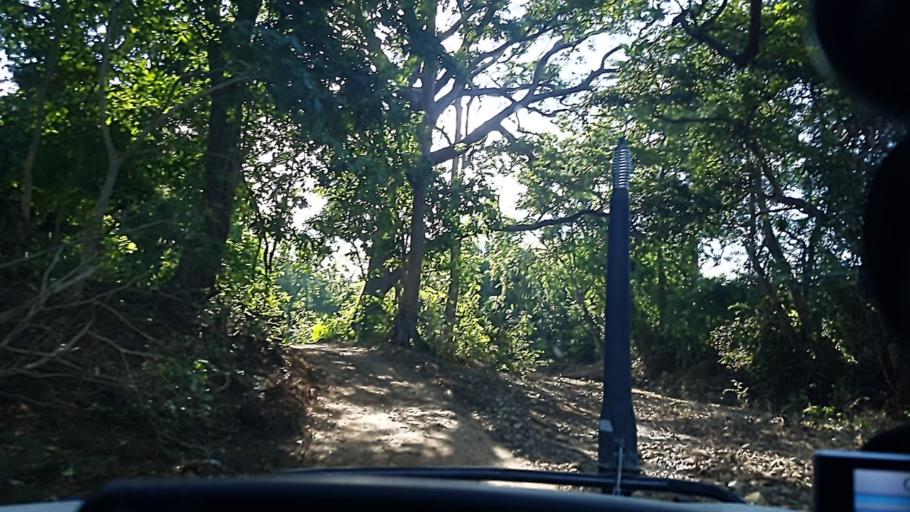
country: NI
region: Rivas
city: Tola
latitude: 11.5350
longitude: -86.1331
